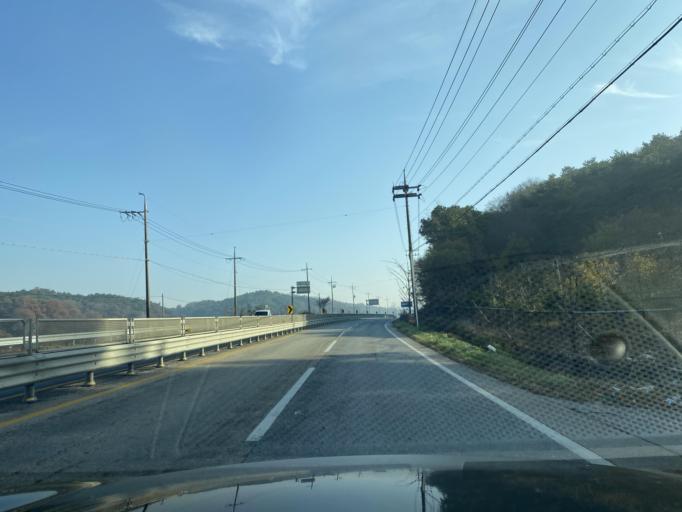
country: KR
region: Chungcheongnam-do
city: Yesan
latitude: 36.7469
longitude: 126.8676
